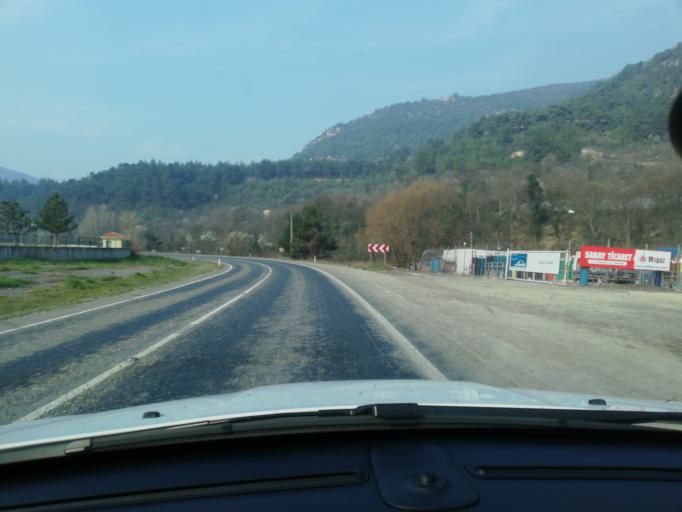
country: TR
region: Karabuk
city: Karabuk
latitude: 41.1726
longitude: 32.5804
